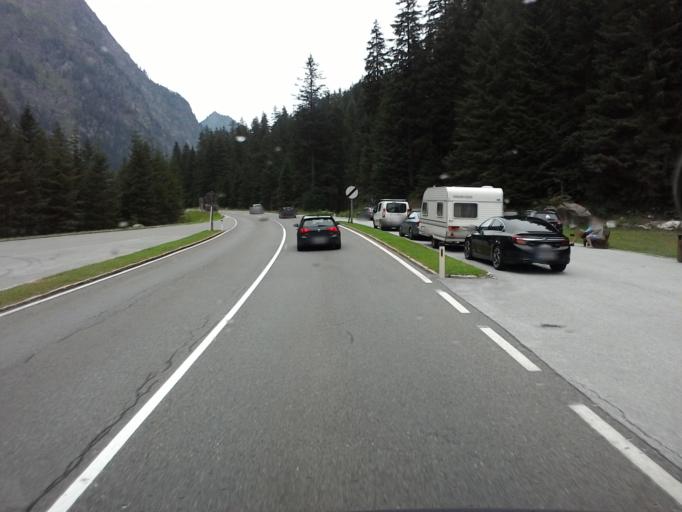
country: AT
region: Salzburg
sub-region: Politischer Bezirk Zell am See
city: Stuhlfelden
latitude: 47.1800
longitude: 12.5297
